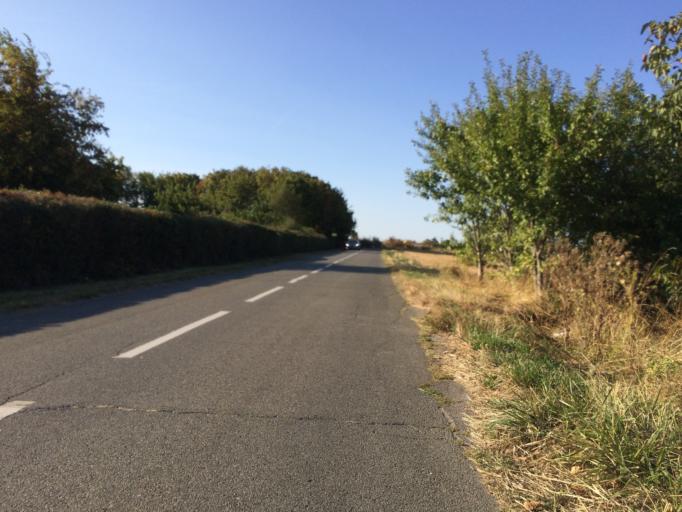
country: FR
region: Ile-de-France
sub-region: Departement de l'Essonne
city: Villiers-sur-Orge
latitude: 48.6668
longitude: 2.3045
